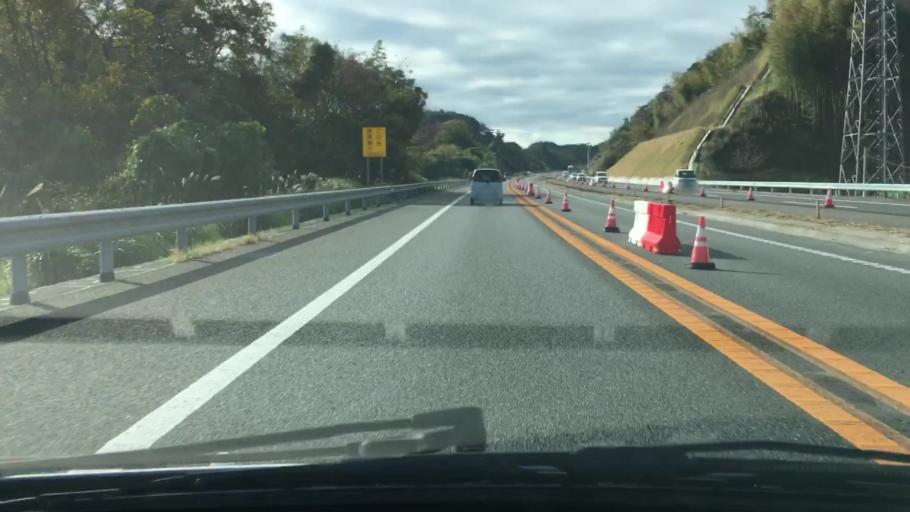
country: JP
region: Chiba
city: Kimitsu
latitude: 35.2789
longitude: 139.9240
